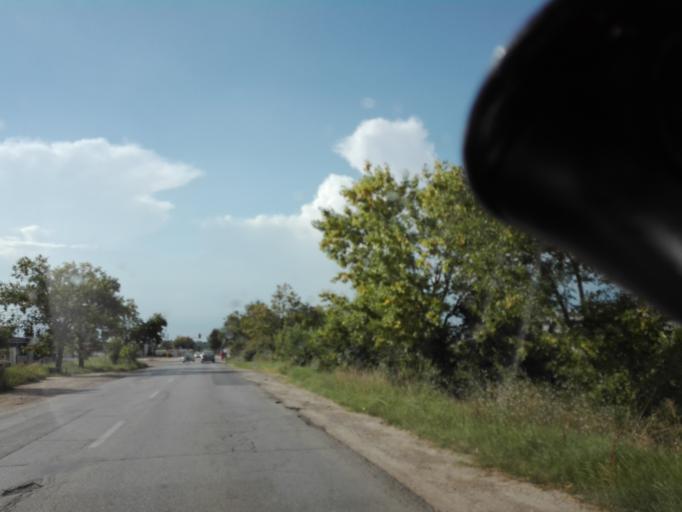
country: BG
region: Sofia-Capital
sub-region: Stolichna Obshtina
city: Sofia
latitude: 42.6254
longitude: 23.4471
